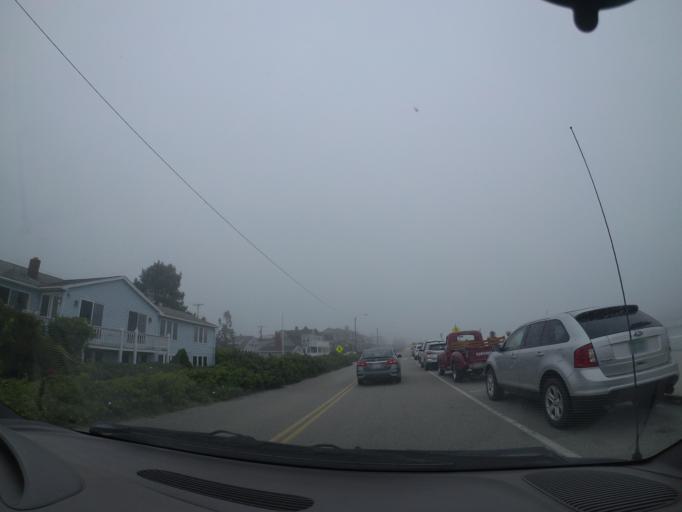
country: US
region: Maine
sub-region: York County
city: Kennebunkport
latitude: 43.3476
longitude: -70.4833
